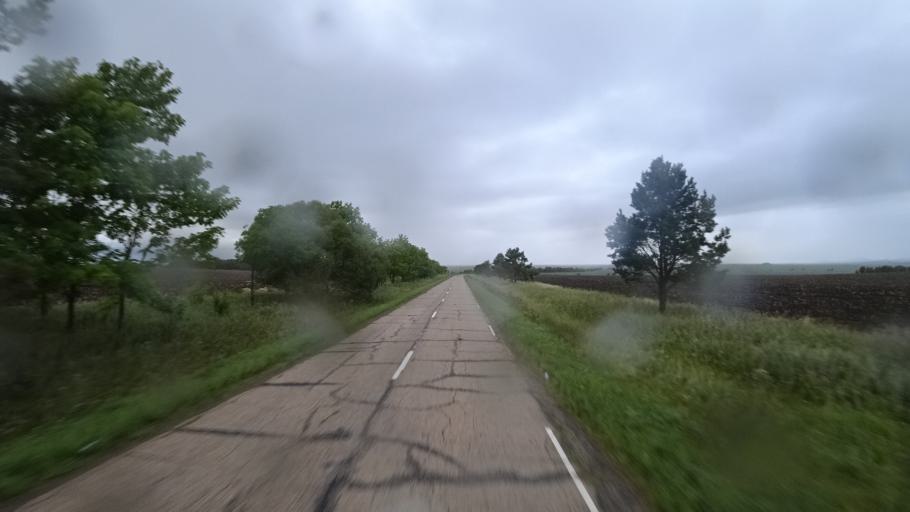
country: RU
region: Primorskiy
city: Chernigovka
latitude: 44.3687
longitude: 132.5325
